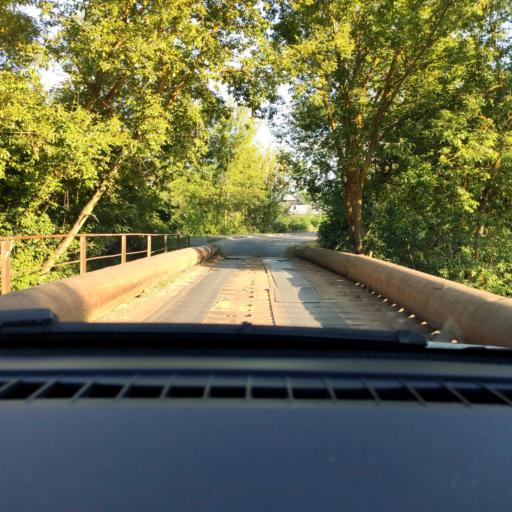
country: RU
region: Voronezj
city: Devitsa
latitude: 51.6421
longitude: 38.9465
